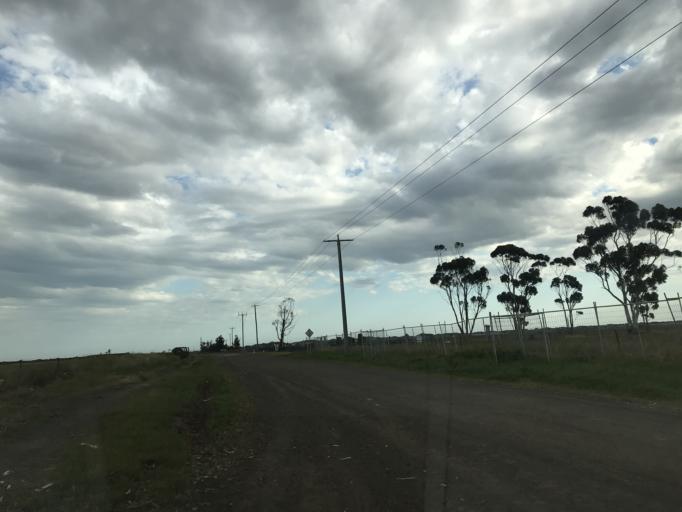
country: AU
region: Victoria
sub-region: Wyndham
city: Truganina
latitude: -37.8246
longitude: 144.7212
